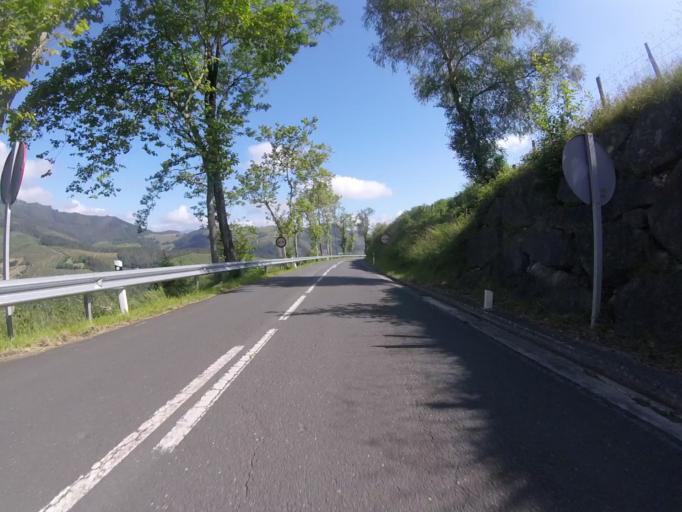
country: ES
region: Basque Country
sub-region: Provincia de Guipuzcoa
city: Ormaiztegui
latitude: 43.0910
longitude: -2.2431
